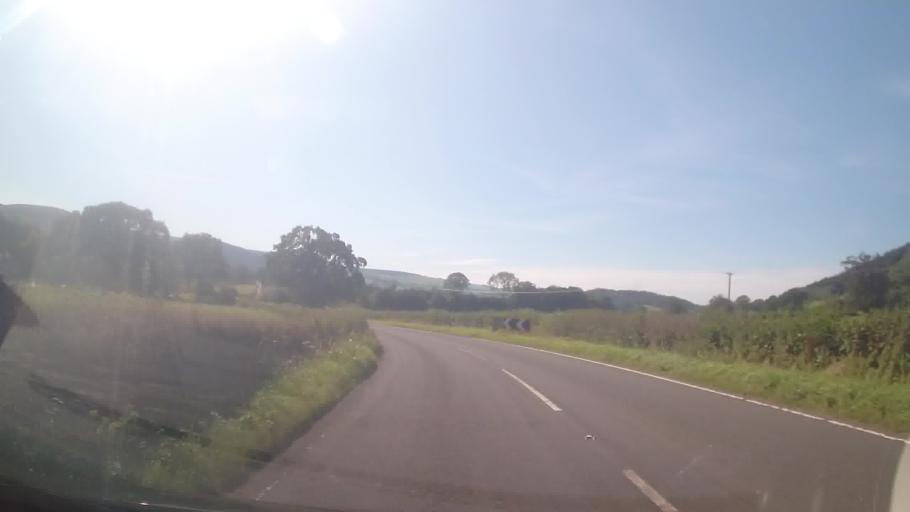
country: GB
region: Wales
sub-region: Sir Powys
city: Montgomery
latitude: 52.5259
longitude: -3.1452
